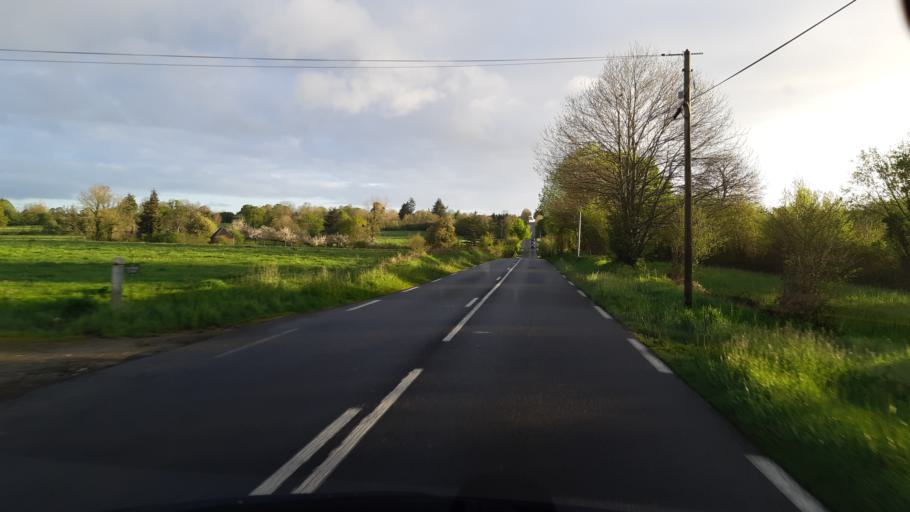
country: FR
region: Lower Normandy
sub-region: Departement de la Manche
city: Tessy-sur-Vire
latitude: 49.0191
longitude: -1.1474
